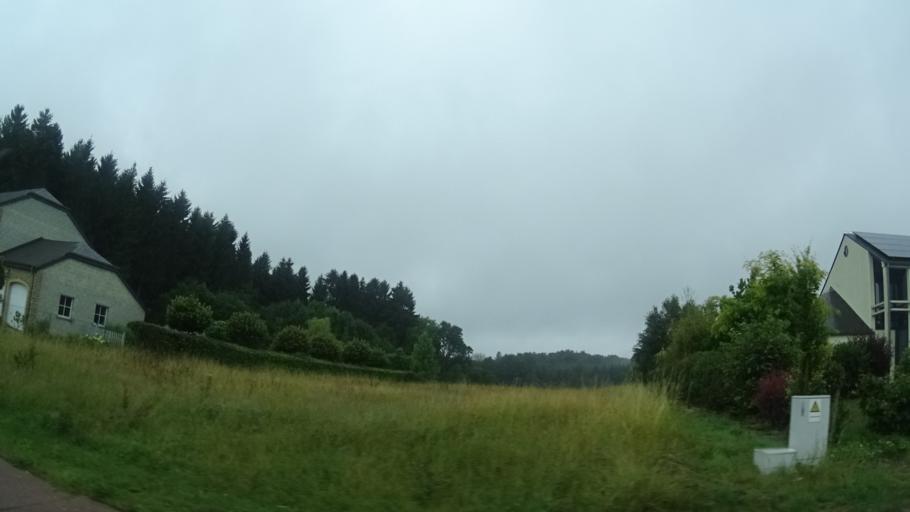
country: BE
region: Wallonia
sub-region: Province du Luxembourg
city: Habay-la-Vieille
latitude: 49.7251
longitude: 5.6333
